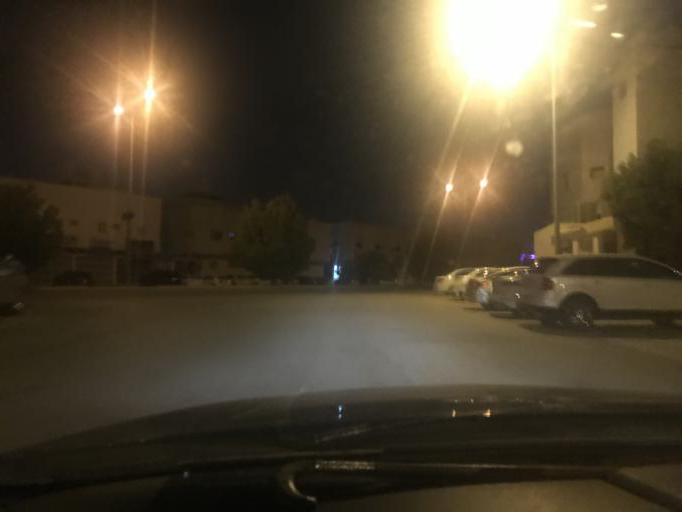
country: SA
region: Ar Riyad
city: Riyadh
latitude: 24.7588
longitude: 46.7614
